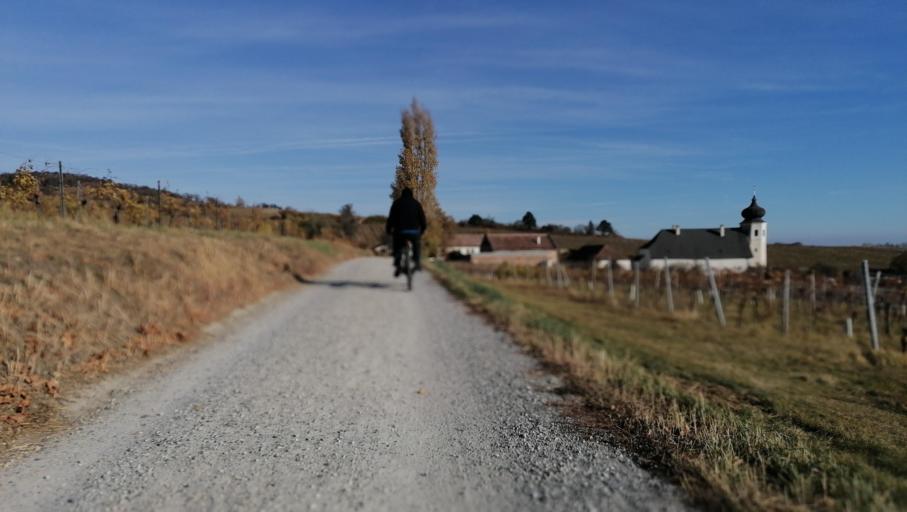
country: AT
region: Lower Austria
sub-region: Politischer Bezirk Modling
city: Gumpoldskirchen
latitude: 48.0509
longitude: 16.2902
